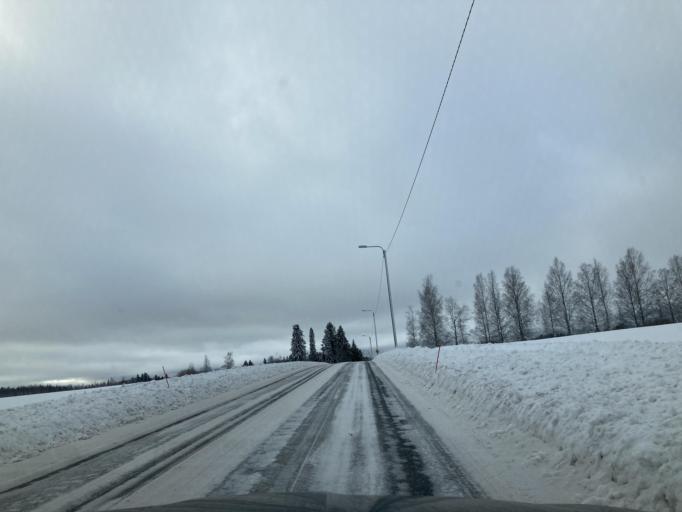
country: FI
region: Central Finland
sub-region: Jaemsae
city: Jaemsae
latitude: 61.8609
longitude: 25.2303
